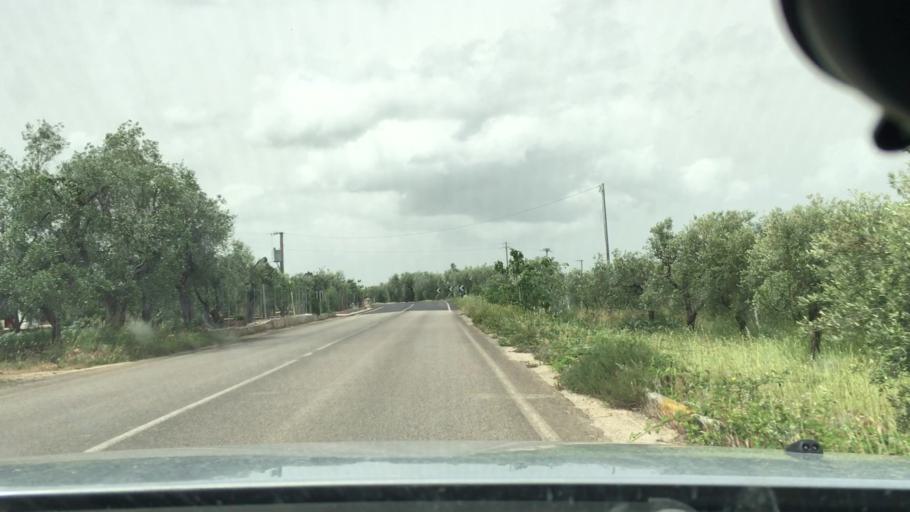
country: IT
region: Apulia
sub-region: Provincia di Bari
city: Capurso
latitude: 41.0414
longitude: 16.9472
